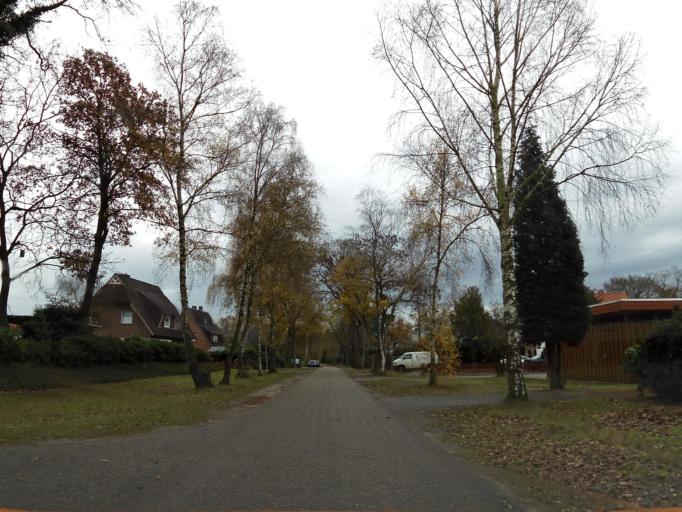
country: DE
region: Lower Saxony
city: Hude
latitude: 53.1013
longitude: 8.4728
